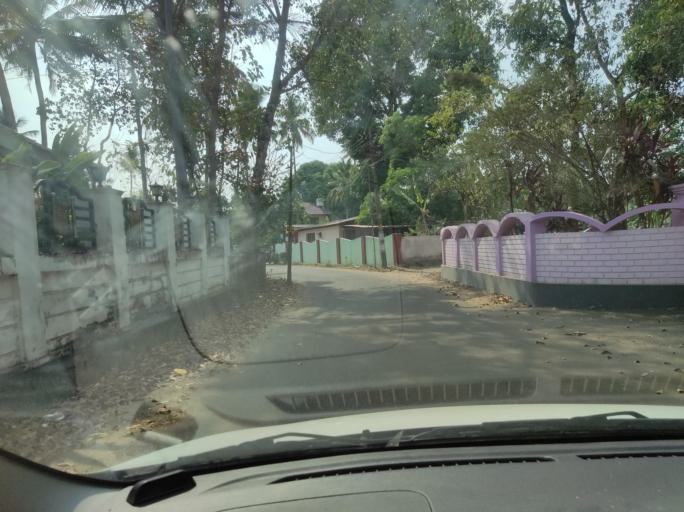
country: IN
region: Kerala
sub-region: Kottayam
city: Kottayam
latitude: 9.6857
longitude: 76.5025
